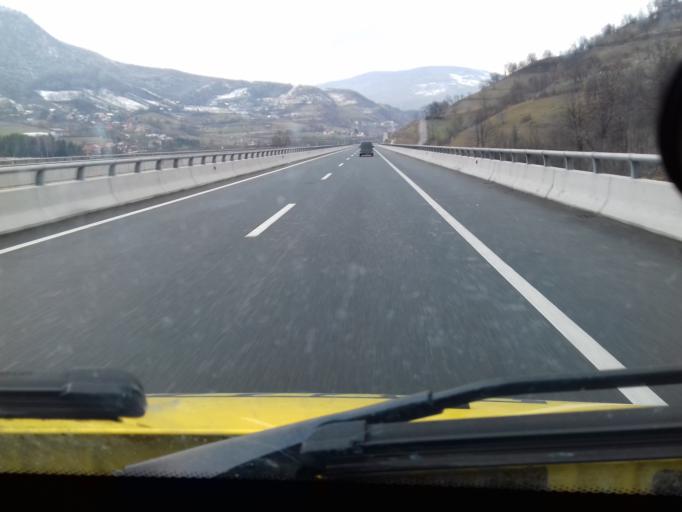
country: BA
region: Federation of Bosnia and Herzegovina
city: Zenica
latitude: 44.1536
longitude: 17.9660
